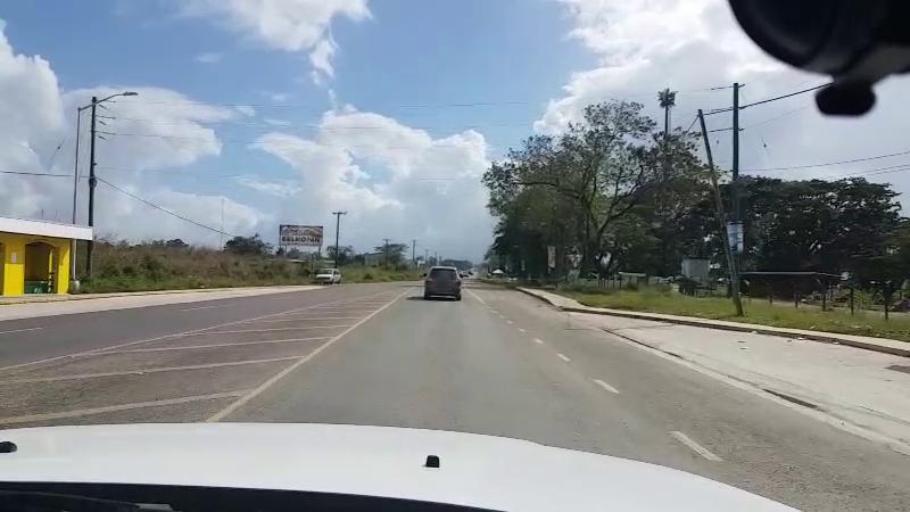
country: BZ
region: Cayo
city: Belmopan
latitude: 17.2605
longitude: -88.7873
